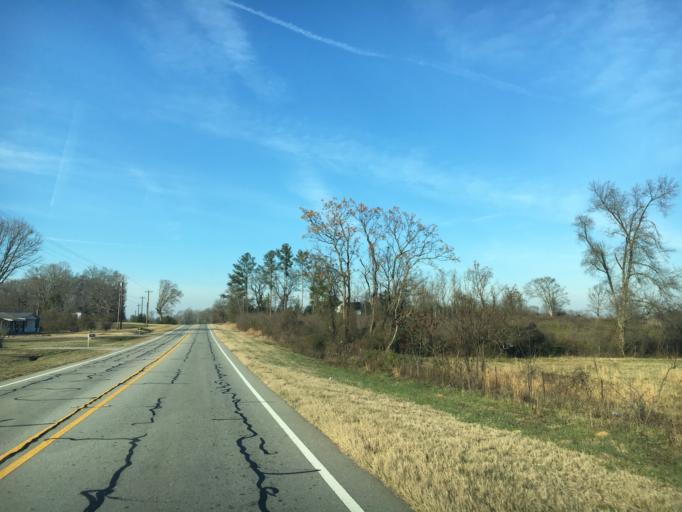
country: US
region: Georgia
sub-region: Franklin County
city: Lavonia
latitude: 34.4211
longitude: -83.0264
